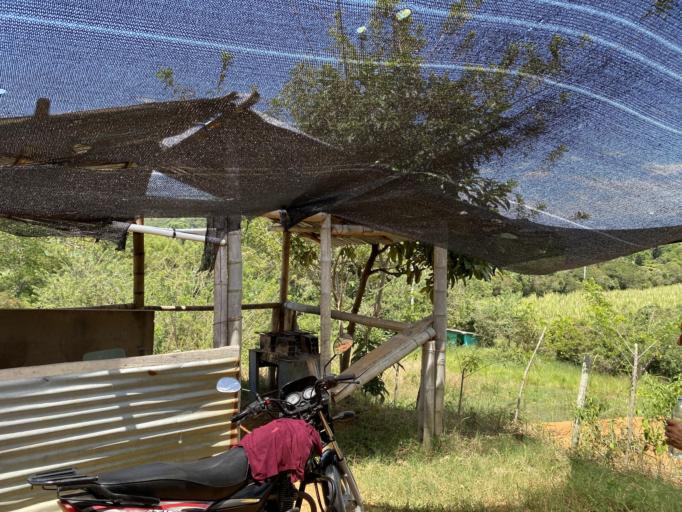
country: CO
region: Valle del Cauca
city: Jamundi
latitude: 3.2921
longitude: -76.5689
